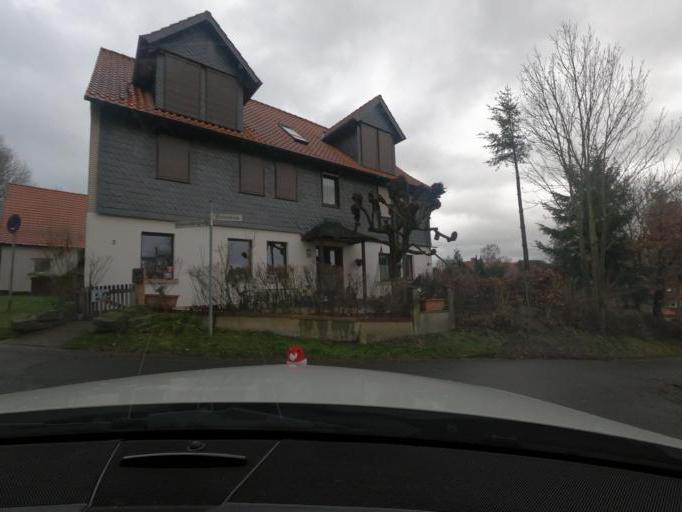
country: DE
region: Lower Saxony
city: Bad Gandersheim
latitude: 51.8494
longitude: 10.0903
